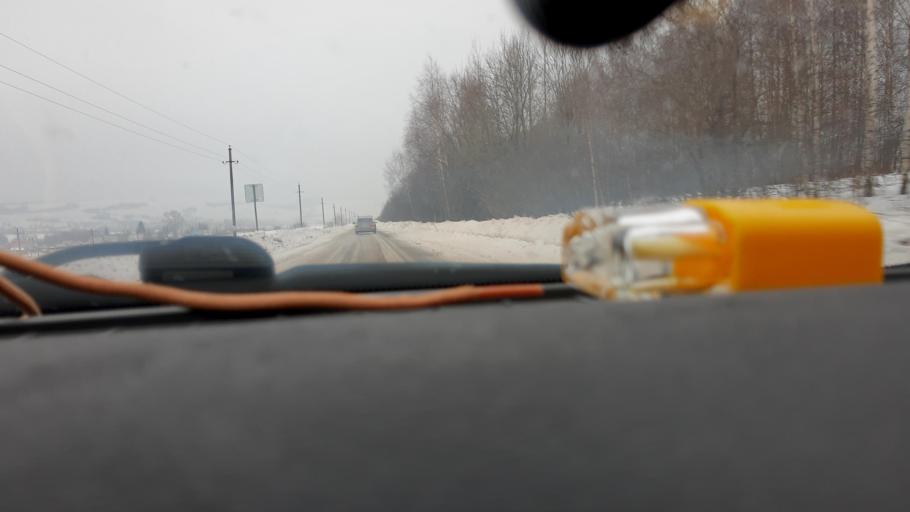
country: RU
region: Bashkortostan
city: Ulukulevo
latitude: 54.5630
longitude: 56.4330
